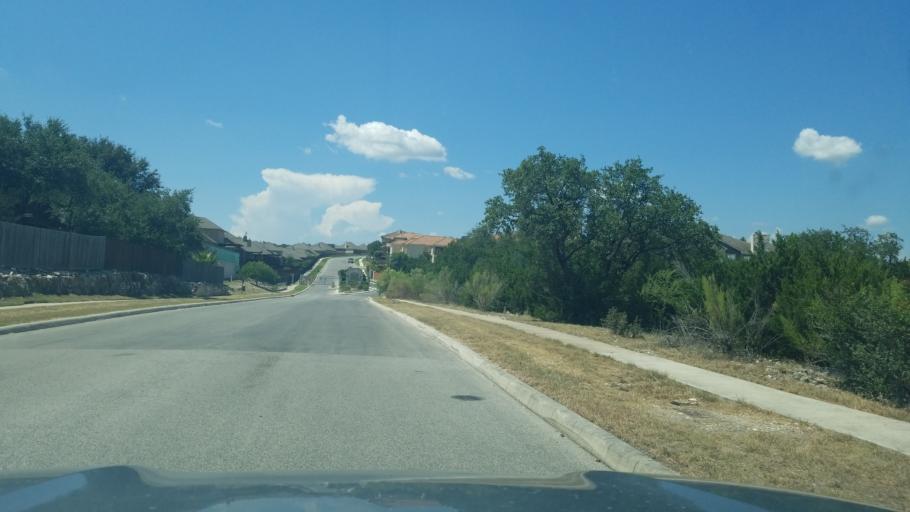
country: US
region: Texas
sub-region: Bexar County
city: Timberwood Park
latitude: 29.6689
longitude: -98.4869
